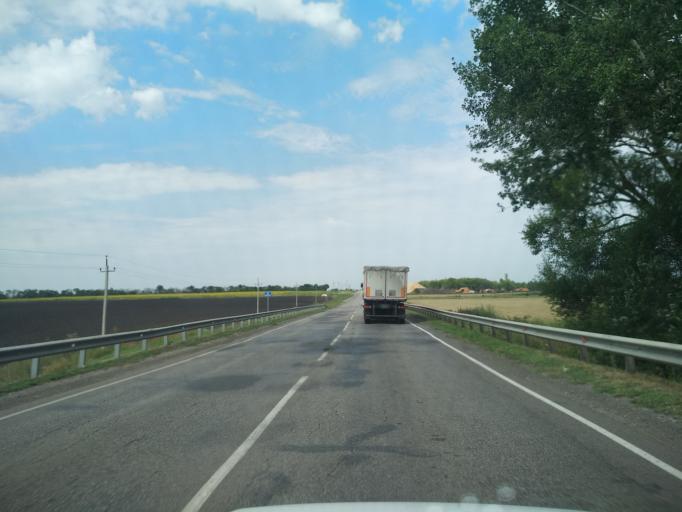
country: RU
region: Voronezj
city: Verkhnyaya Khava
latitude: 51.6778
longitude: 39.8604
